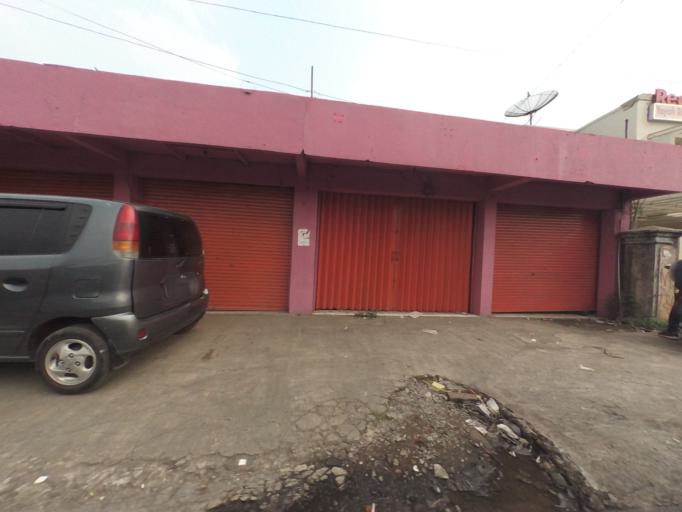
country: ID
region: West Java
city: Ciampea
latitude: -6.5575
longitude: 106.6928
